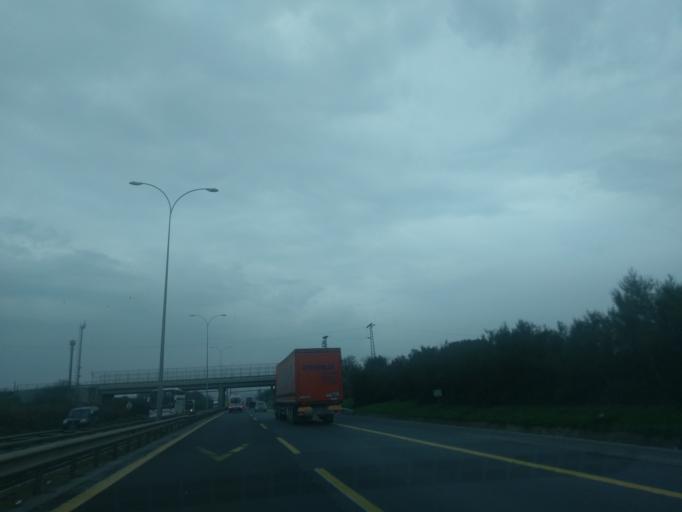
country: TR
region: Istanbul
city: Muratbey
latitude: 41.1066
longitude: 28.5449
